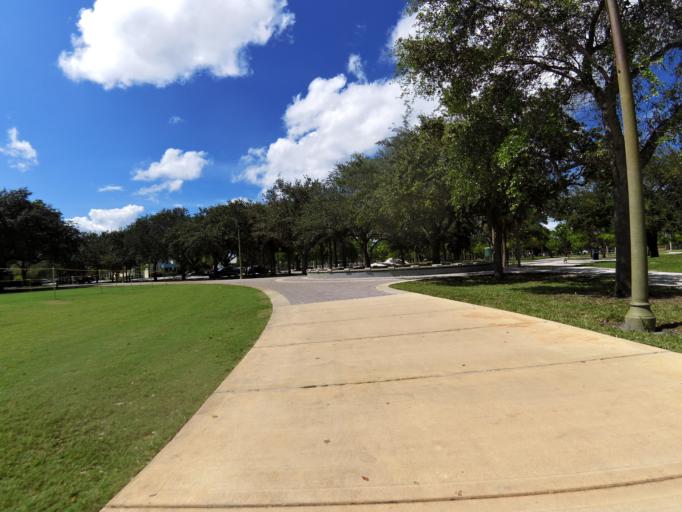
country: US
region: Florida
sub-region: Broward County
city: Fort Lauderdale
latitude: 26.1335
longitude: -80.1308
